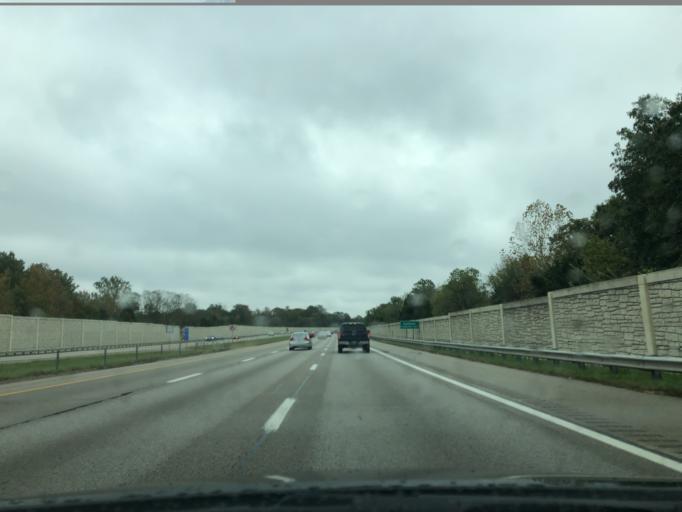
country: US
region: Ohio
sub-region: Hamilton County
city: The Village of Indian Hill
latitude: 39.2518
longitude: -84.3174
